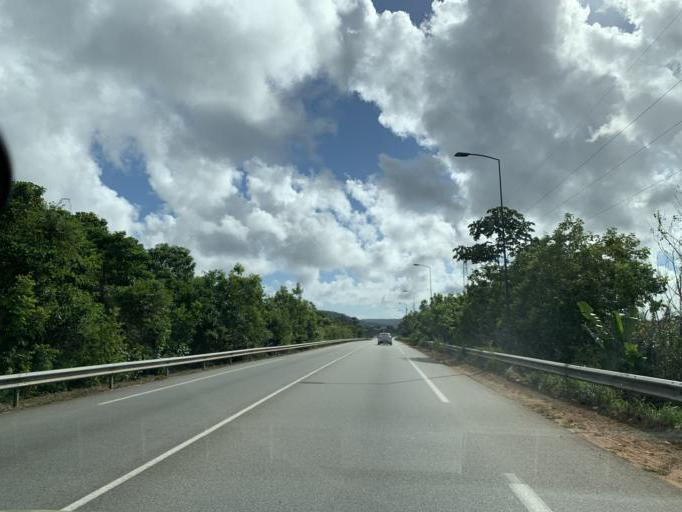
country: GF
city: Macouria
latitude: 4.8915
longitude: -52.3421
